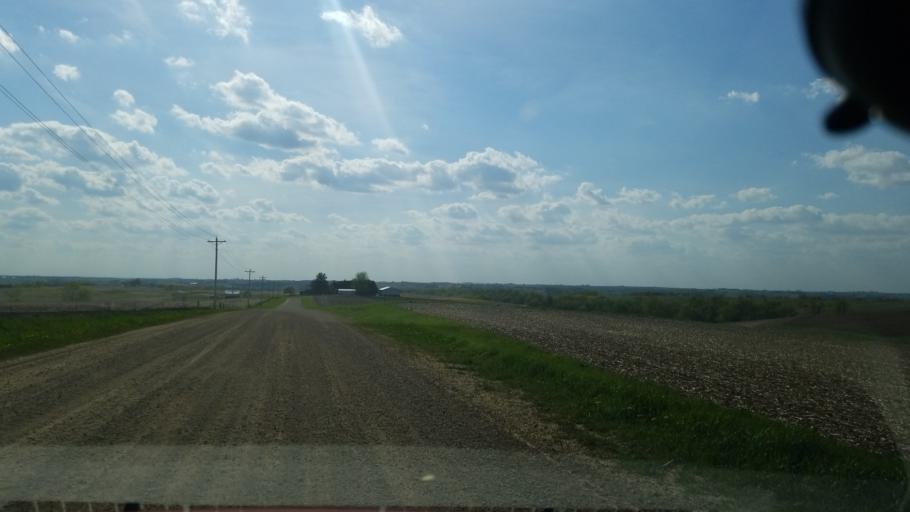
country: US
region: Iowa
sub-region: Jackson County
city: Maquoketa
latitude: 42.2150
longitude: -90.7225
